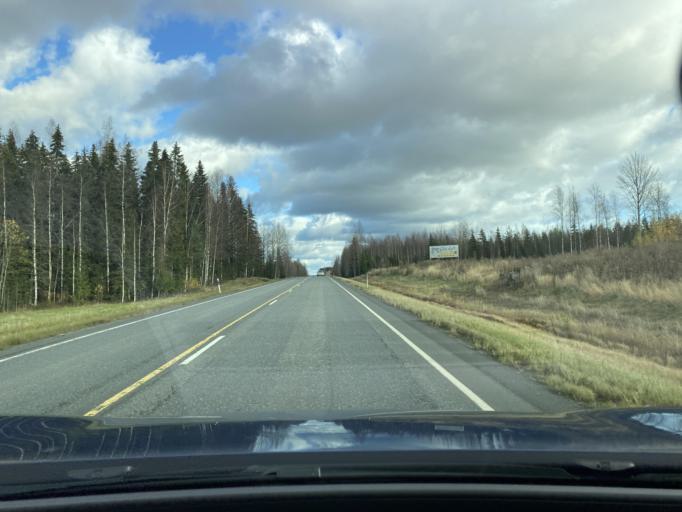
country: FI
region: Haeme
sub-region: Forssa
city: Humppila
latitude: 60.9426
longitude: 23.2921
